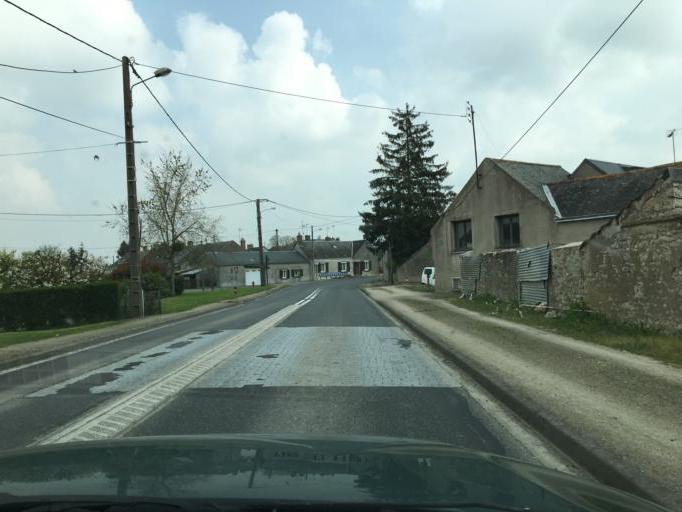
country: FR
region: Centre
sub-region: Departement du Loiret
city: Epieds-en-Beauce
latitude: 47.9286
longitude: 1.5762
